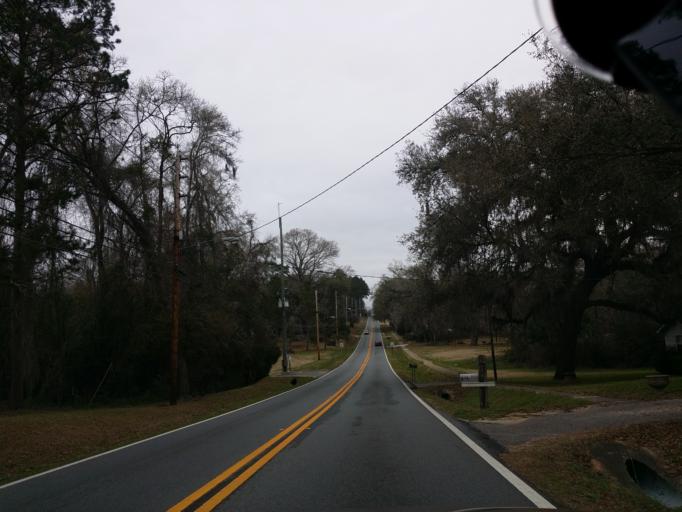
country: US
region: Florida
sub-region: Leon County
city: Tallahassee
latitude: 30.4908
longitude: -84.2299
